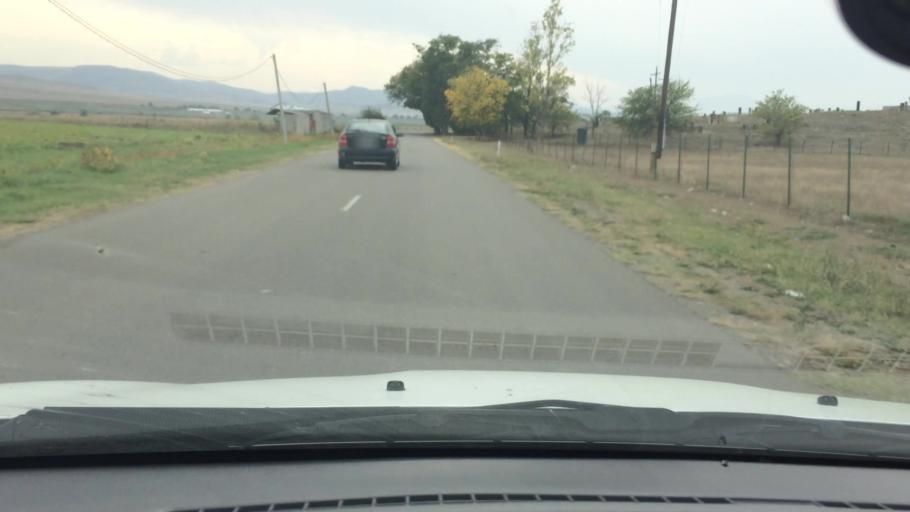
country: AM
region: Tavush
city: Berdavan
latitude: 41.3508
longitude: 44.9608
